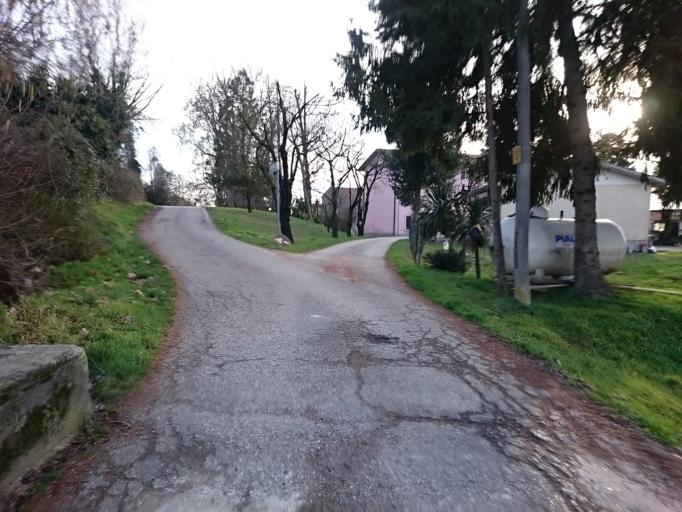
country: IT
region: Veneto
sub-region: Provincia di Verona
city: Cavalcaselle
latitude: 45.4520
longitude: 10.7273
